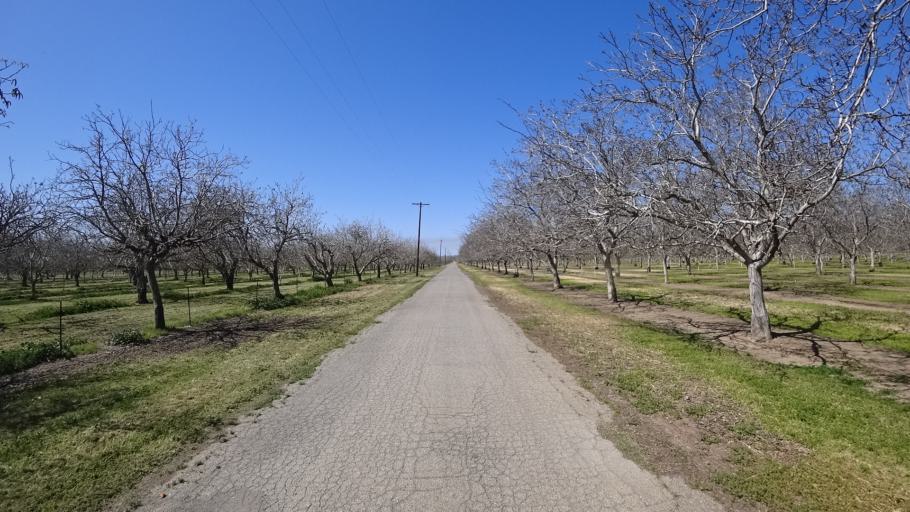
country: US
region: California
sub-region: Glenn County
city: Willows
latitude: 39.4435
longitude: -121.9775
